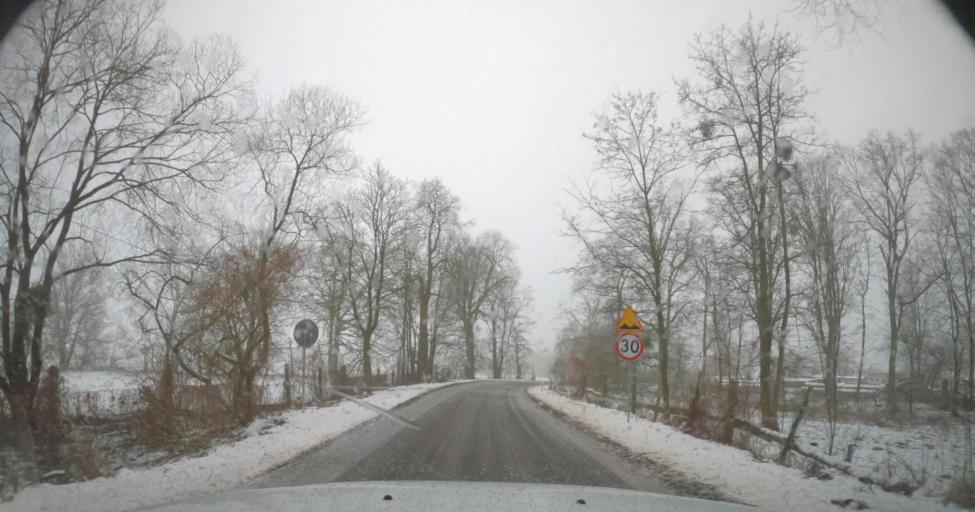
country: PL
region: West Pomeranian Voivodeship
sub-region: Powiat goleniowski
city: Stepnica
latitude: 53.5653
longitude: 14.6817
